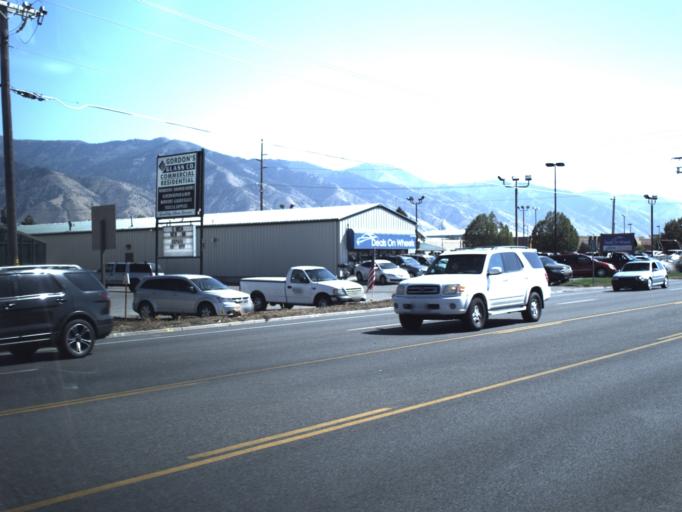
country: US
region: Utah
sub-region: Cache County
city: North Logan
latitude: 41.7663
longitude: -111.8343
